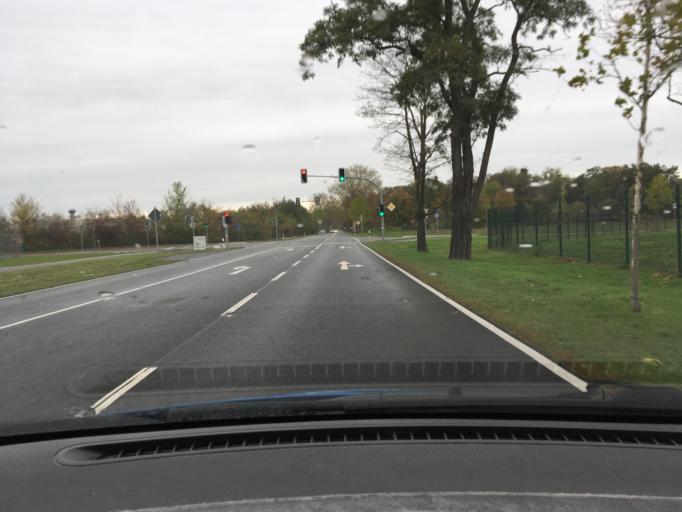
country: DE
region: Saxony-Anhalt
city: Rodleben
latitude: 51.9030
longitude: 12.2115
